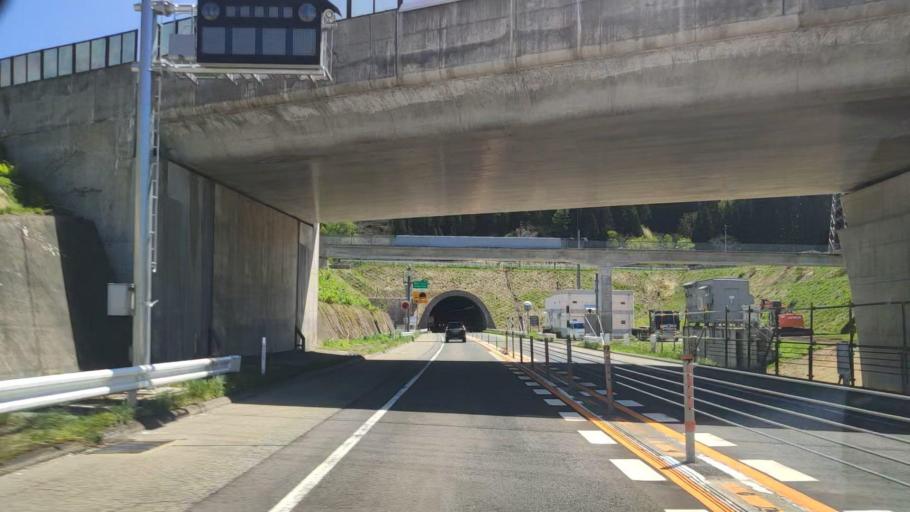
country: JP
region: Yamagata
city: Shinjo
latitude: 38.6901
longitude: 140.3128
